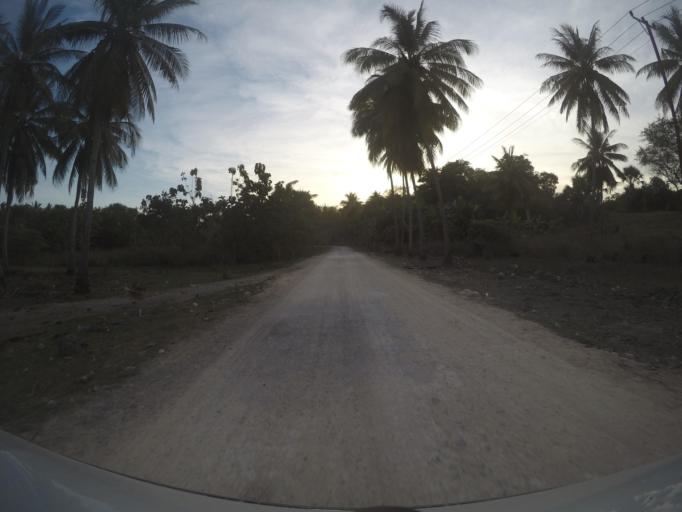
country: TL
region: Viqueque
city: Viqueque
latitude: -8.9416
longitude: 126.4373
